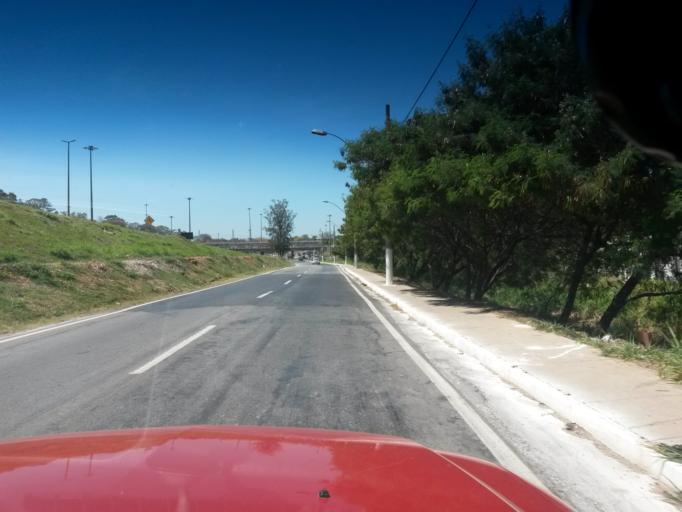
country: BR
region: Minas Gerais
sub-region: Belo Horizonte
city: Belo Horizonte
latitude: -19.8896
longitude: -43.9719
